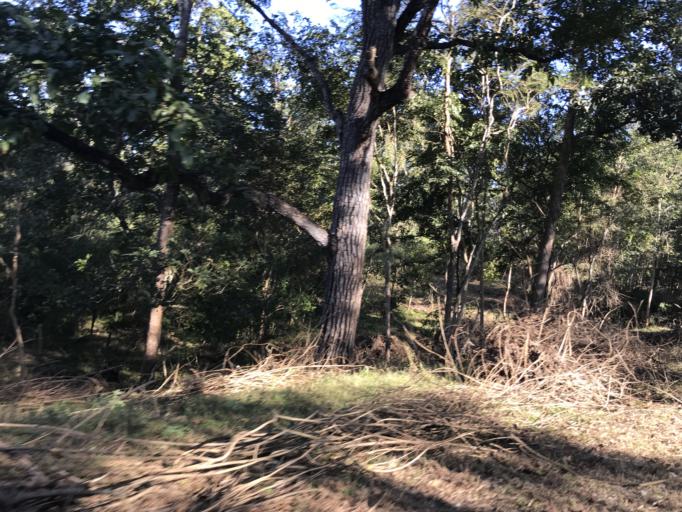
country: IN
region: Karnataka
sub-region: Mysore
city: Heggadadevankote
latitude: 11.9804
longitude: 76.2334
